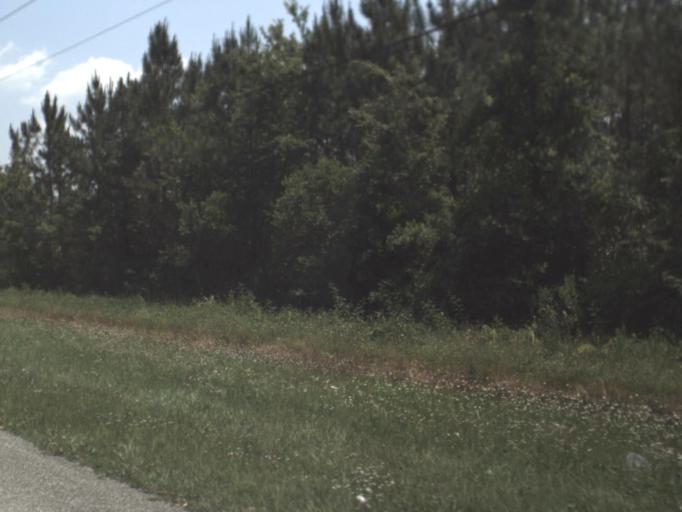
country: US
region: Florida
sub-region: Duval County
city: Baldwin
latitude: 30.2744
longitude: -81.9866
